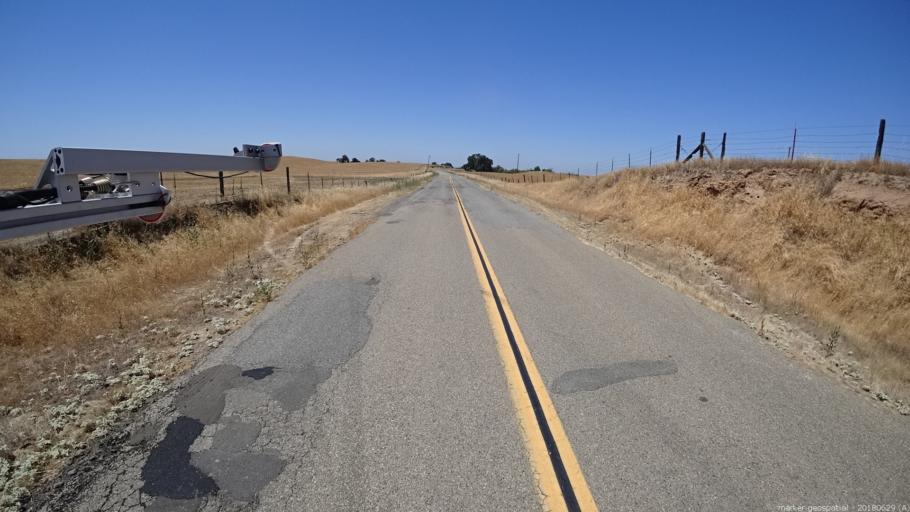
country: US
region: California
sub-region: Madera County
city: Bonadelle Ranchos-Madera Ranchos
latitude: 37.0775
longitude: -119.8971
